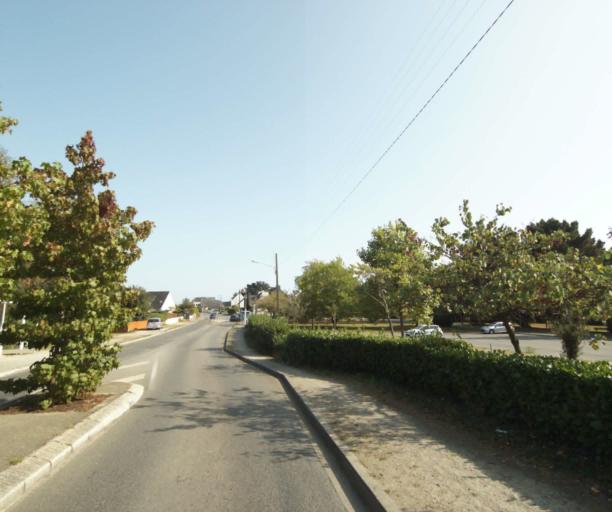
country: FR
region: Brittany
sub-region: Departement du Morbihan
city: Riantec
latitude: 47.7192
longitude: -3.3173
